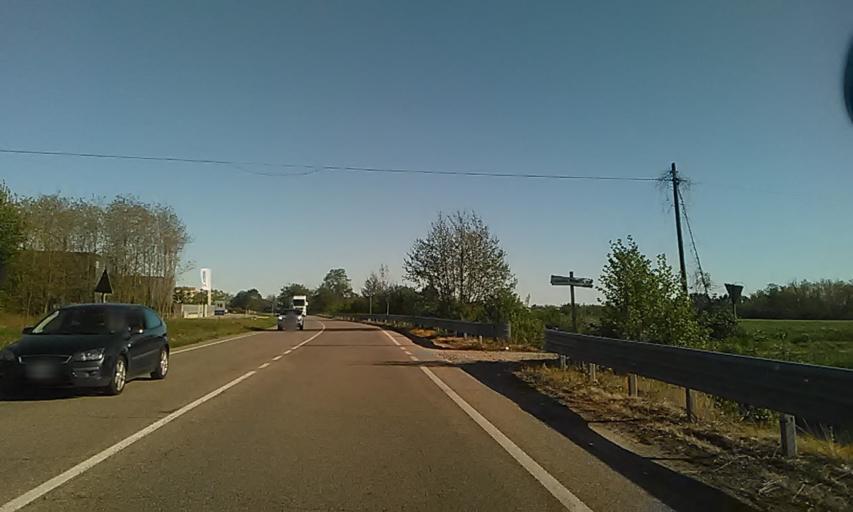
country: IT
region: Piedmont
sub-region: Provincia di Novara
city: Vaprio D'Agogna
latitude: 45.5956
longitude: 8.5375
